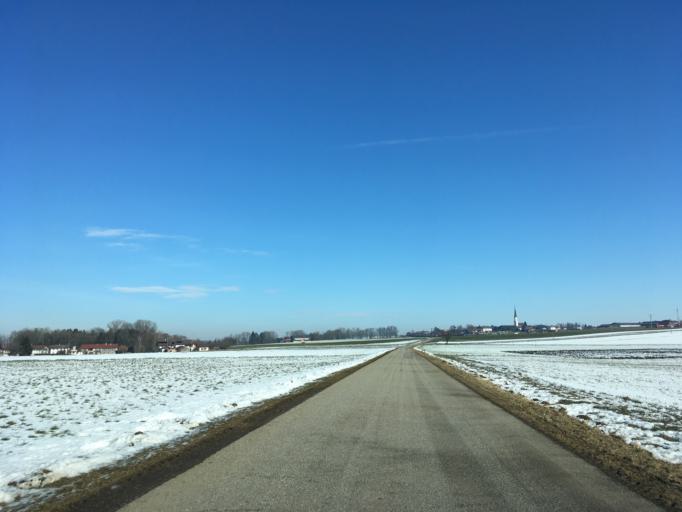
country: DE
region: Bavaria
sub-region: Upper Bavaria
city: Griesstatt
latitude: 47.9835
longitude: 12.1651
